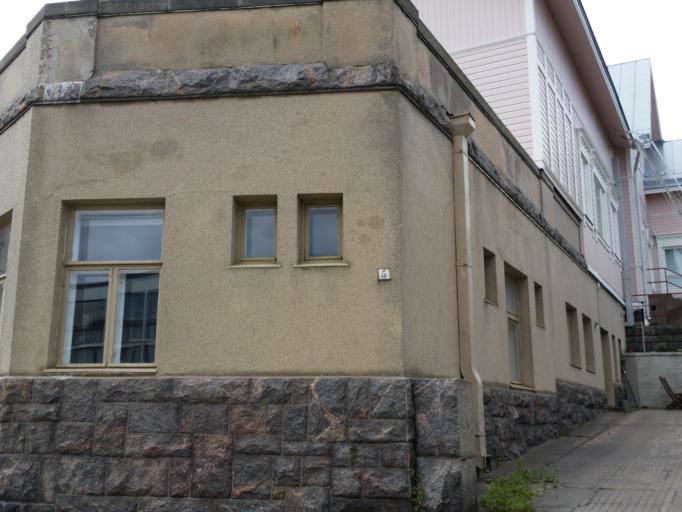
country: FI
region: Uusimaa
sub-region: Raaseporin
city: Hanko
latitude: 59.8227
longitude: 22.9661
